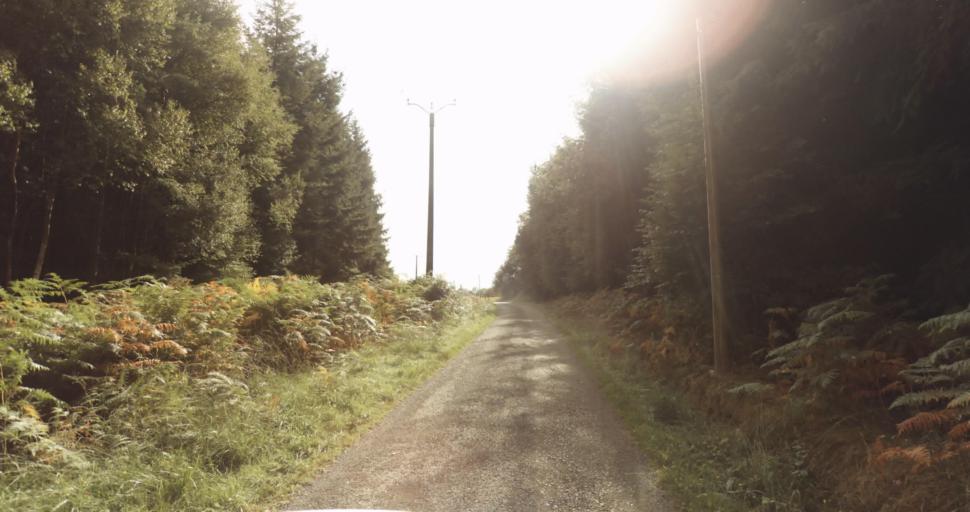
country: FR
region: Lower Normandy
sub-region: Departement de l'Orne
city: Gace
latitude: 48.8370
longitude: 0.3559
